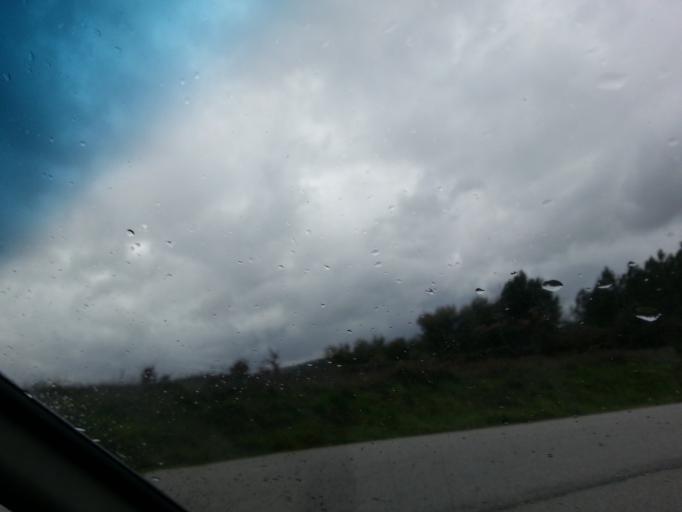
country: PT
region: Viseu
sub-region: Viseu
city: Rio de Loba
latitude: 40.6065
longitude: -7.8537
